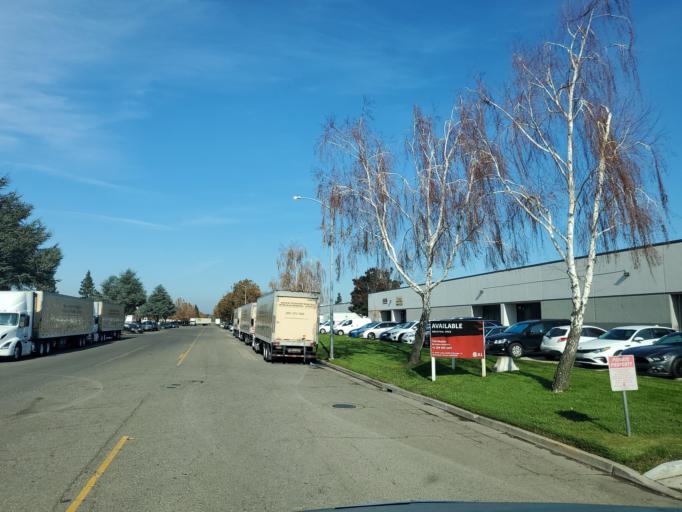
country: US
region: California
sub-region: San Joaquin County
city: Kennedy
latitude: 37.9071
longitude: -121.2130
